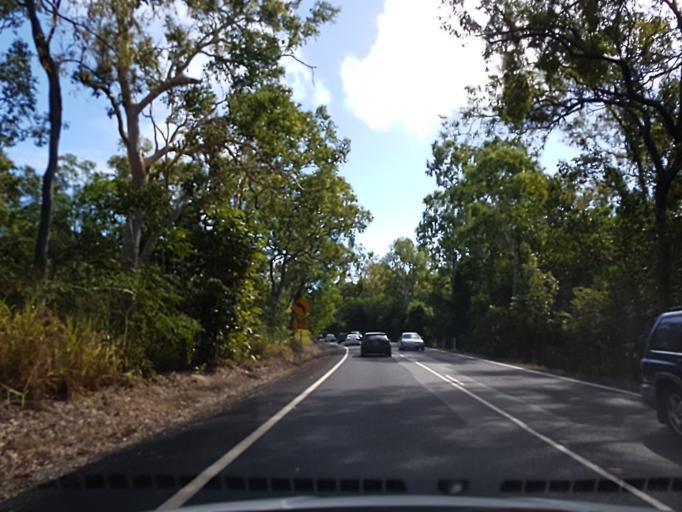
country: AU
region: Queensland
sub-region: Cairns
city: Palm Cove
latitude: -16.6683
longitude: 145.5680
